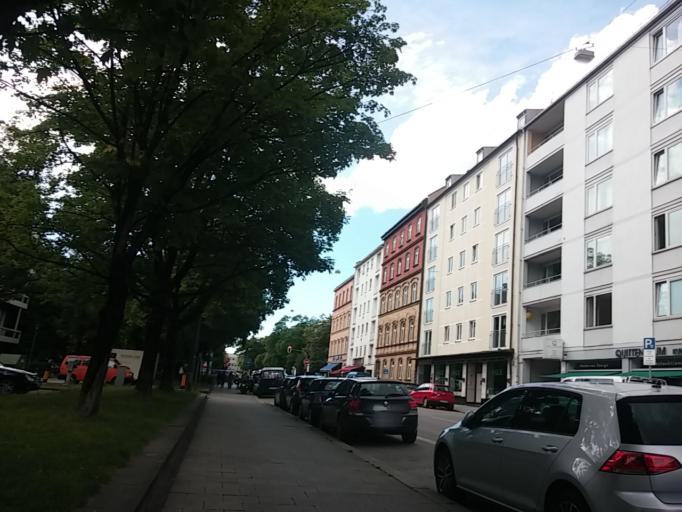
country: DE
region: Bavaria
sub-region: Upper Bavaria
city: Munich
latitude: 48.1485
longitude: 11.5733
